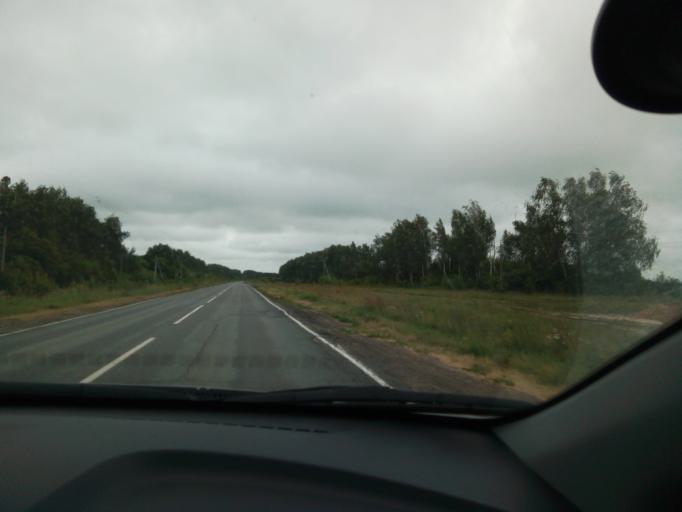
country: RU
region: Chuvashia
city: Alikovo
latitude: 55.6220
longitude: 46.7415
